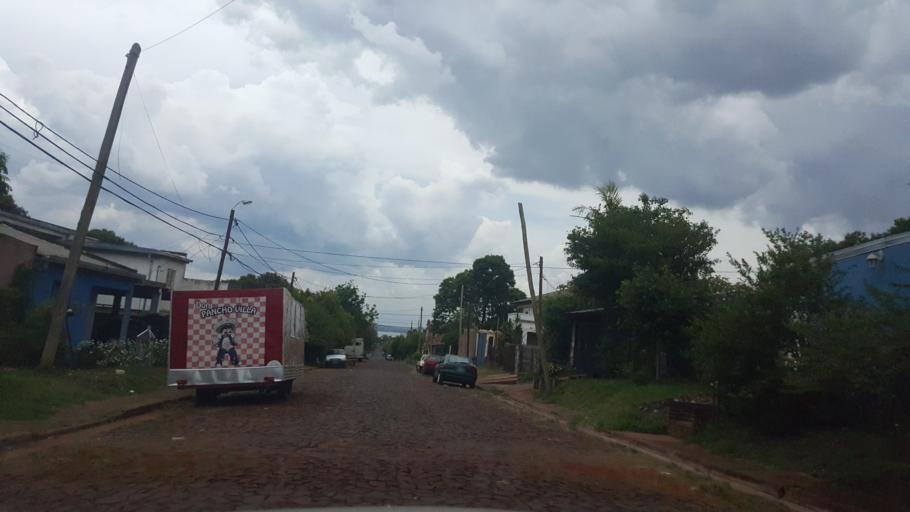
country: AR
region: Misiones
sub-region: Departamento de Capital
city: Posadas
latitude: -27.3892
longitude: -55.9108
